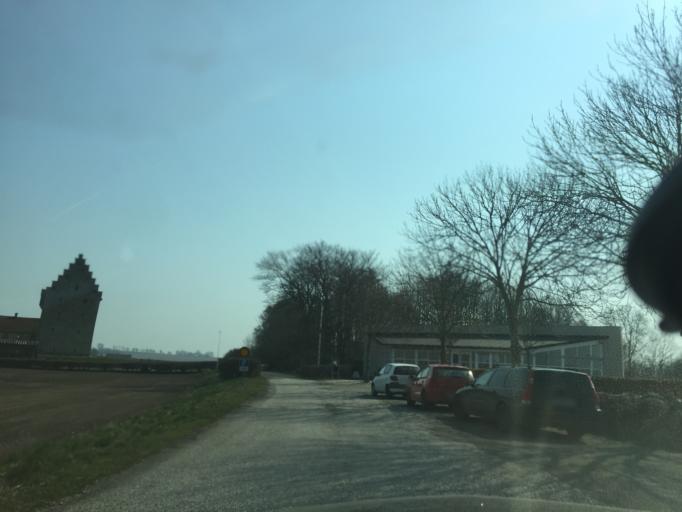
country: SE
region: Skane
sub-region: Simrishamns Kommun
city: Simrishamn
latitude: 55.5013
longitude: 14.2281
